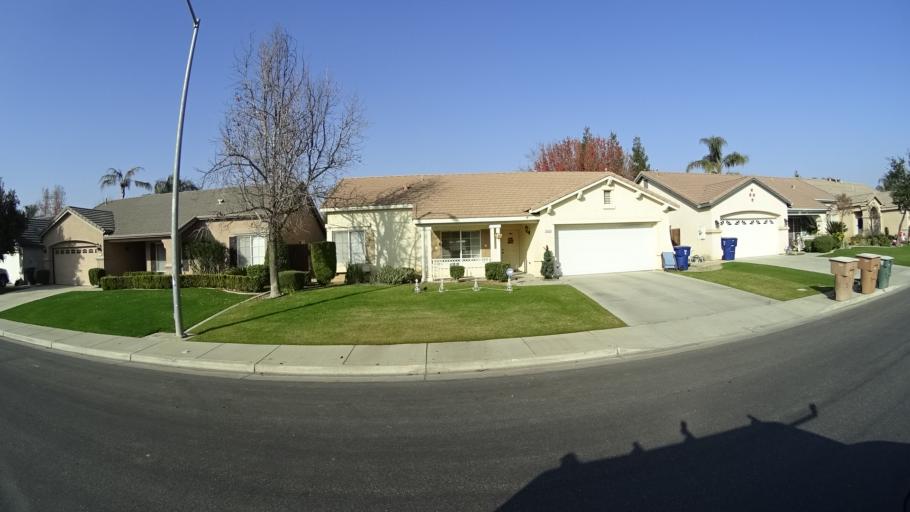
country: US
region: California
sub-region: Kern County
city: Greenacres
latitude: 35.4165
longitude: -119.0959
